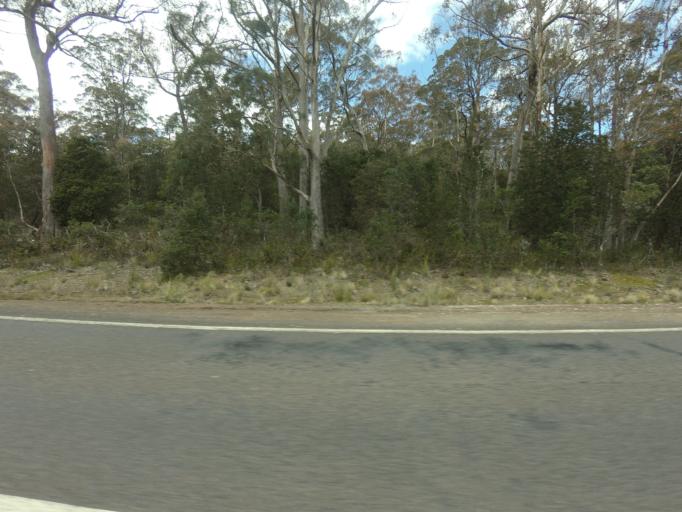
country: AU
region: Tasmania
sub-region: Northern Midlands
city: Evandale
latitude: -42.0102
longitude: 147.7237
